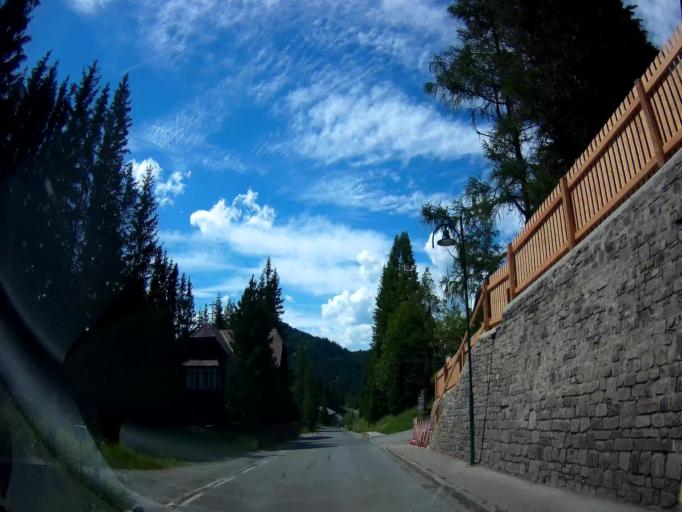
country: AT
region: Carinthia
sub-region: Politischer Bezirk Sankt Veit an der Glan
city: Glodnitz
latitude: 46.9440
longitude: 14.0312
